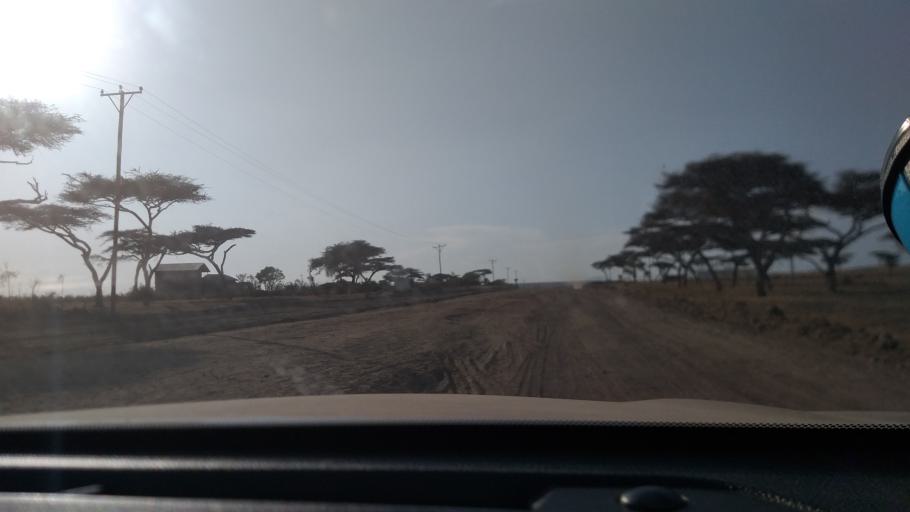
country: ET
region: Oromiya
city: Shashemene
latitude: 7.4979
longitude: 38.6992
